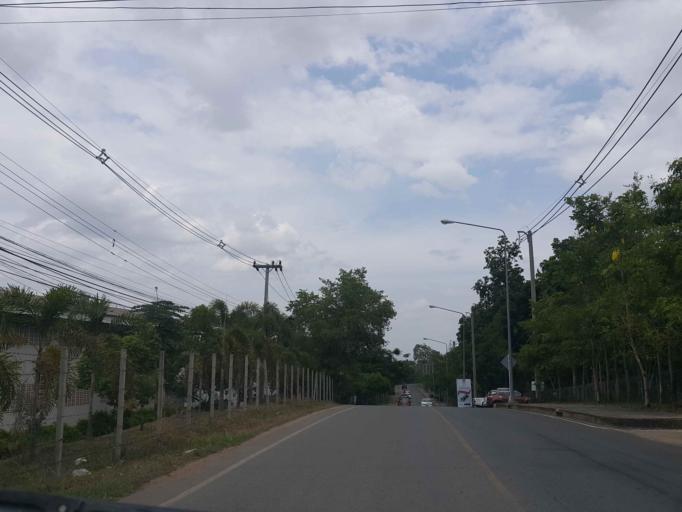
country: TH
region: Chiang Mai
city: Hang Dong
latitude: 18.7542
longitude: 98.9243
